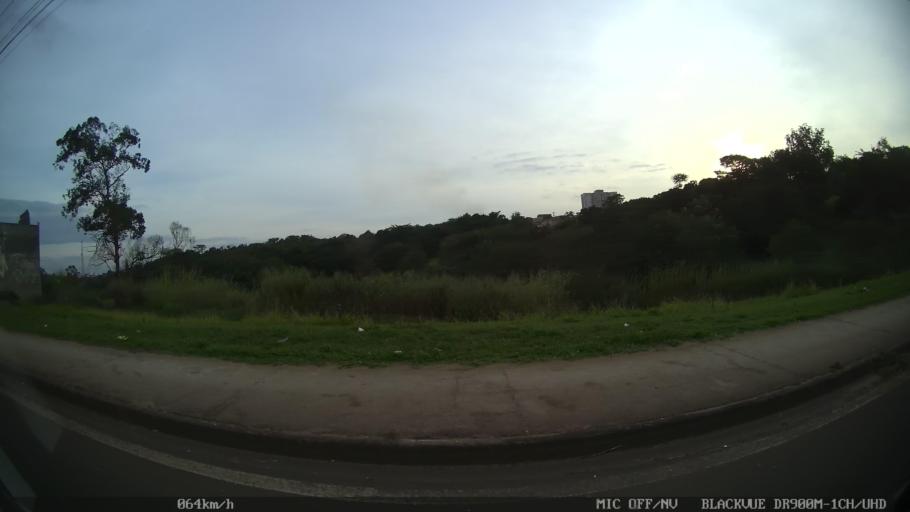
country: BR
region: Sao Paulo
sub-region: Limeira
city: Limeira
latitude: -22.5639
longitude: -47.3810
